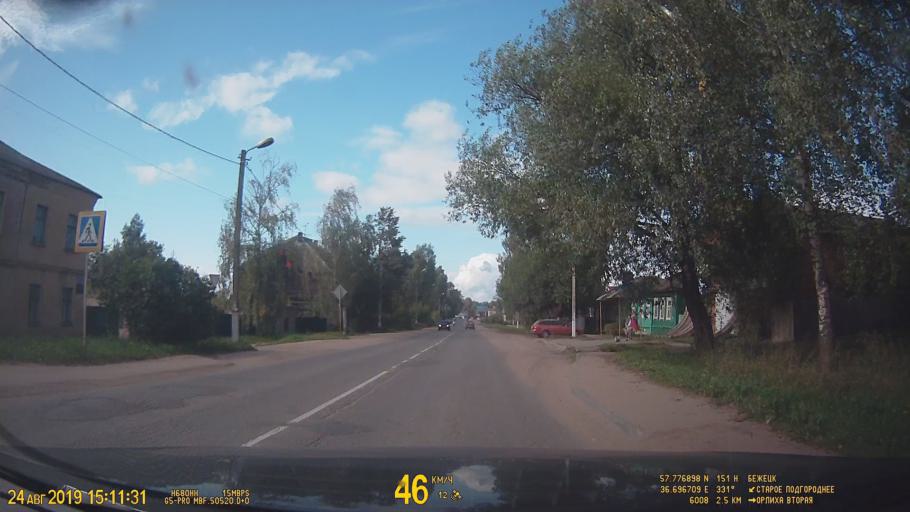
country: RU
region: Tverskaya
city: Bezhetsk
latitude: 57.7770
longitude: 36.6966
